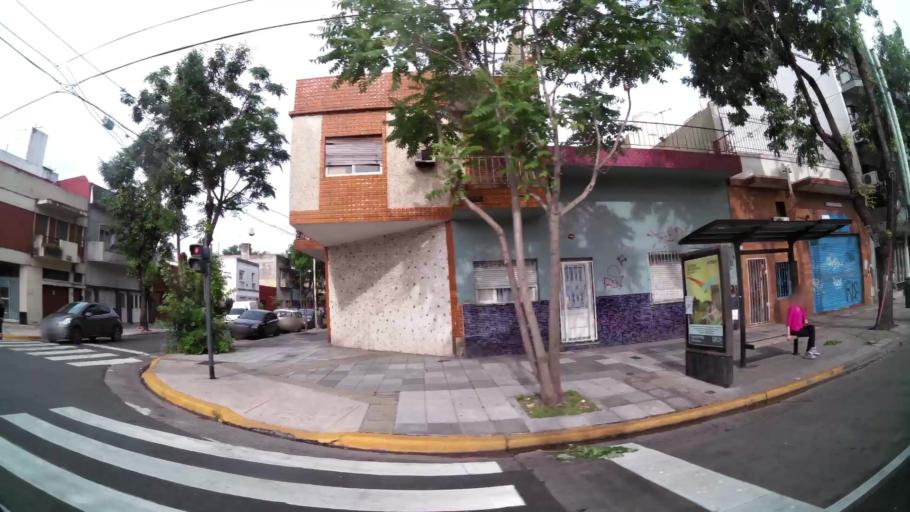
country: AR
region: Buenos Aires F.D.
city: Villa Santa Rita
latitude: -34.6362
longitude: -58.4322
